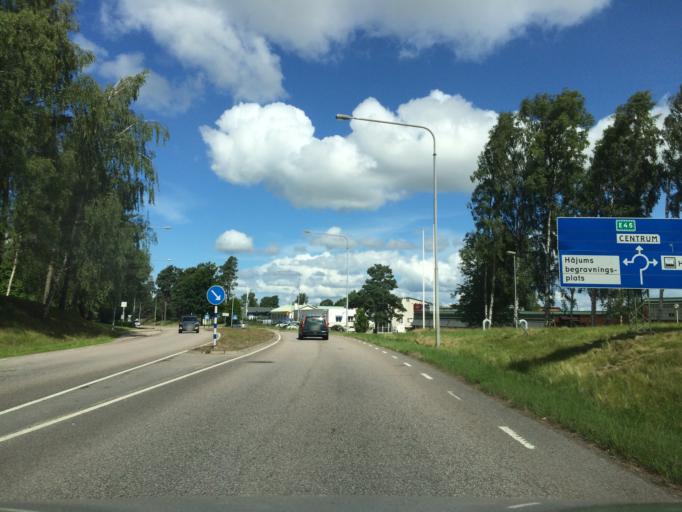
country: SE
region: Vaestra Goetaland
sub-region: Trollhattan
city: Trollhattan
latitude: 58.2779
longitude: 12.3106
